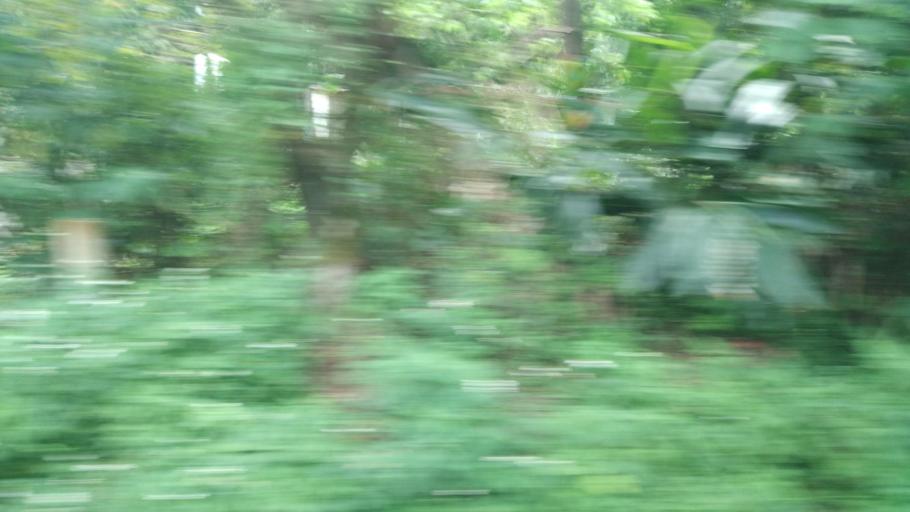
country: TW
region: Taipei
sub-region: Taipei
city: Banqiao
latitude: 24.9262
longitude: 121.4420
